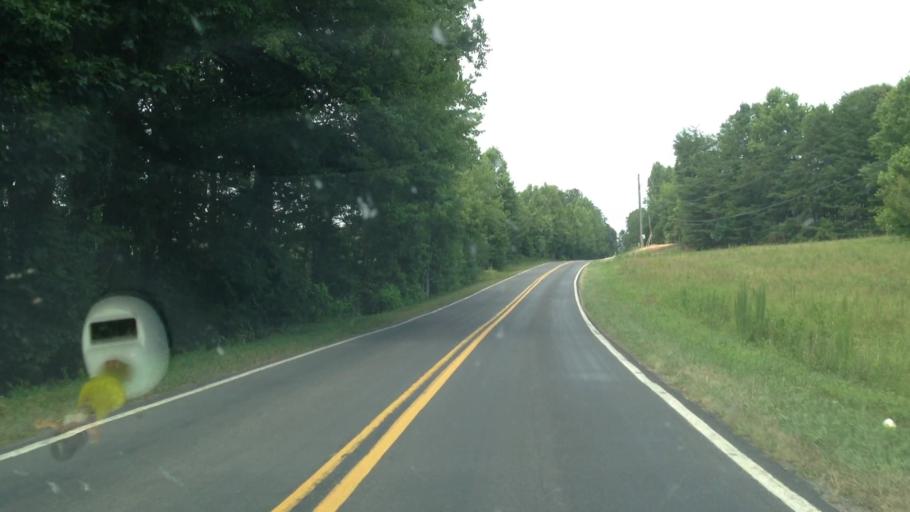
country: US
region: North Carolina
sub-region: Forsyth County
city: Walkertown
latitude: 36.2058
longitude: -80.1082
